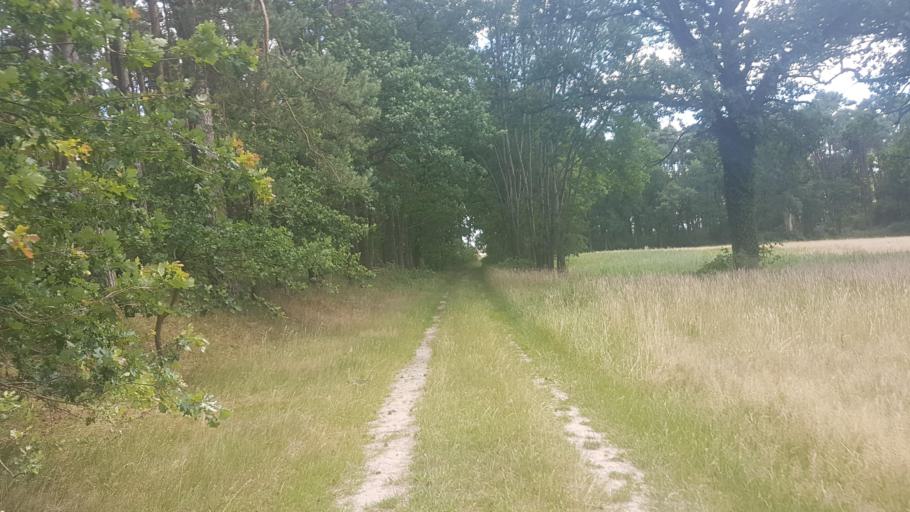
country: DE
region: Lower Saxony
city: Dahlem
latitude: 53.2364
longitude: 10.7700
